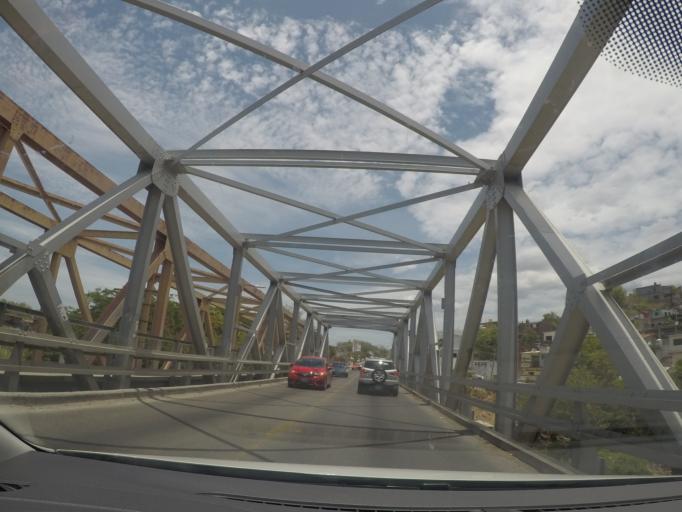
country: MX
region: Oaxaca
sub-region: Santo Domingo Tehuantepec
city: Santo Domingo Tehuantepec
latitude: 16.3291
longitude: -95.2347
